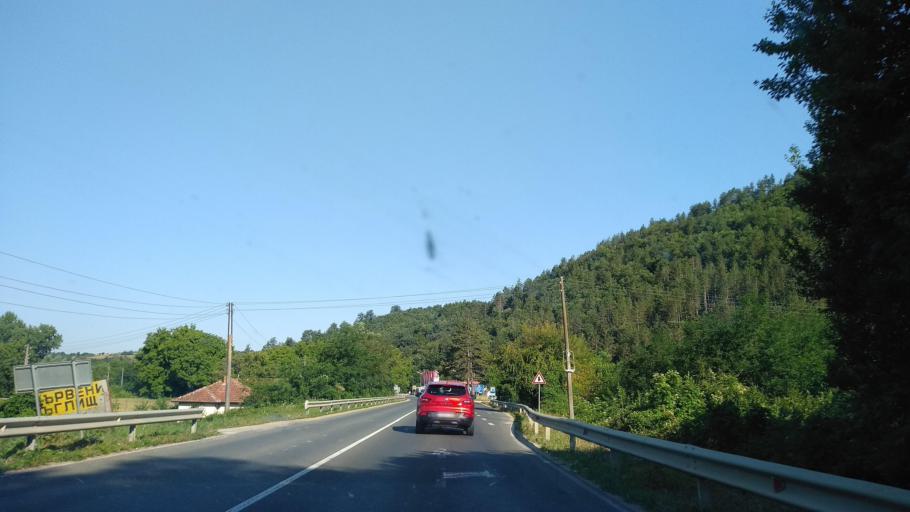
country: BG
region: Lovech
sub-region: Obshtina Yablanitsa
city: Yablanitsa
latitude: 43.0571
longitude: 24.2425
